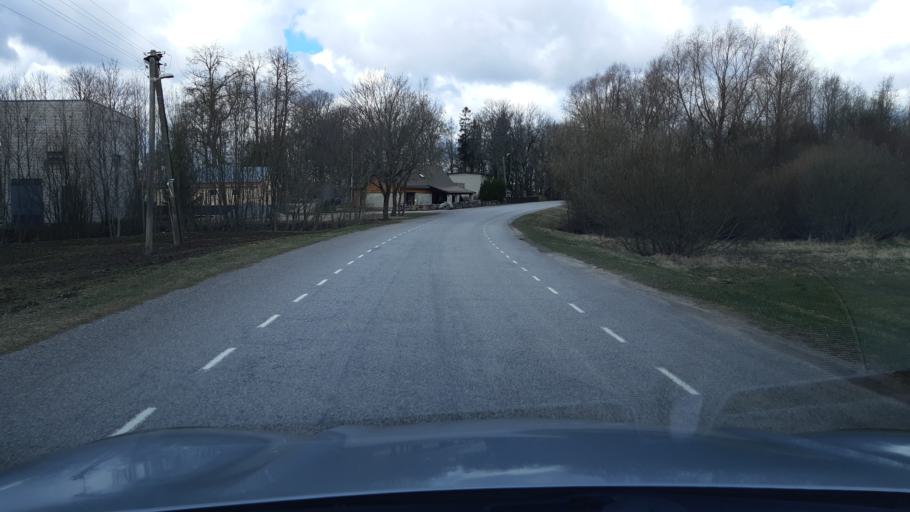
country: EE
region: Raplamaa
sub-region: Kehtna vald
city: Kehtna
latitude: 59.0424
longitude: 25.1199
